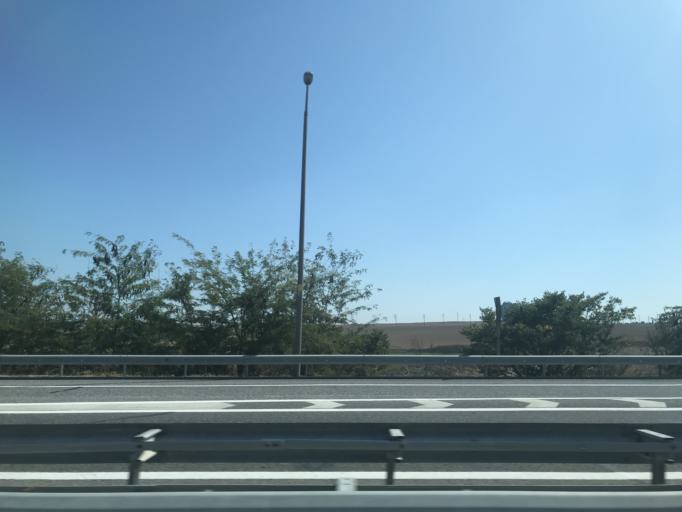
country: TR
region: Kirklareli
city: Luleburgaz
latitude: 41.3939
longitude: 27.3862
